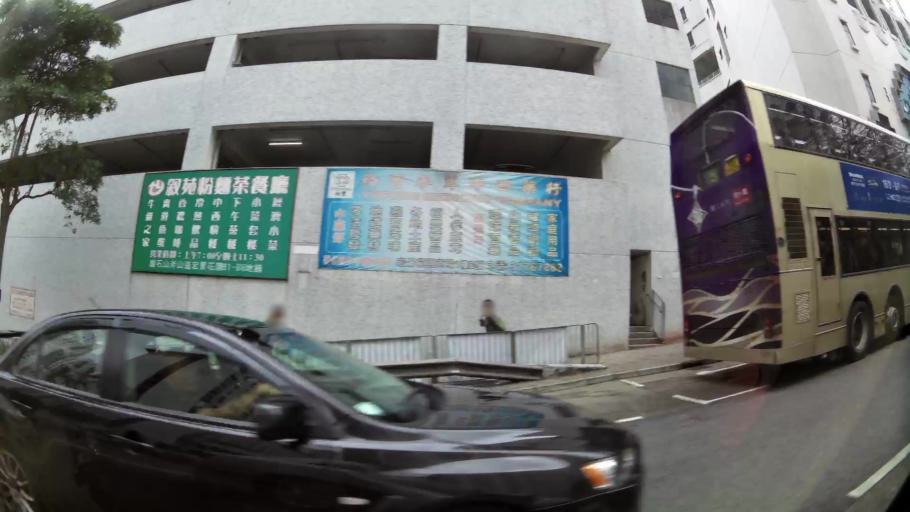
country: HK
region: Wong Tai Sin
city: Wong Tai Sin
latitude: 22.3424
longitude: 114.2081
